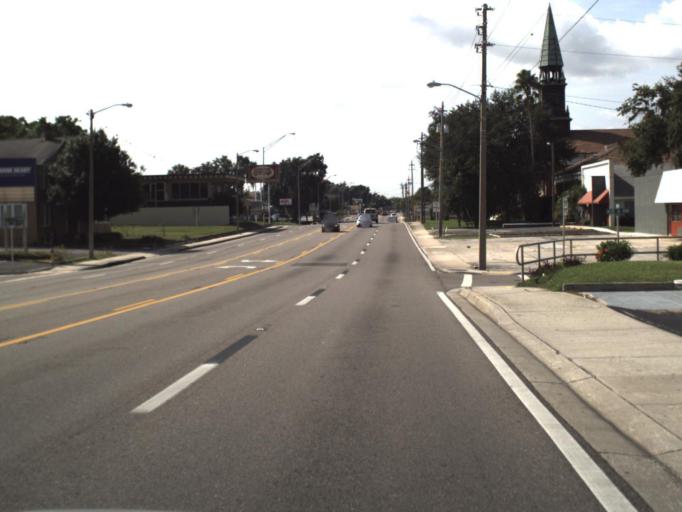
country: US
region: Florida
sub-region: Polk County
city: Winter Haven
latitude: 28.0298
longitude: -81.7330
